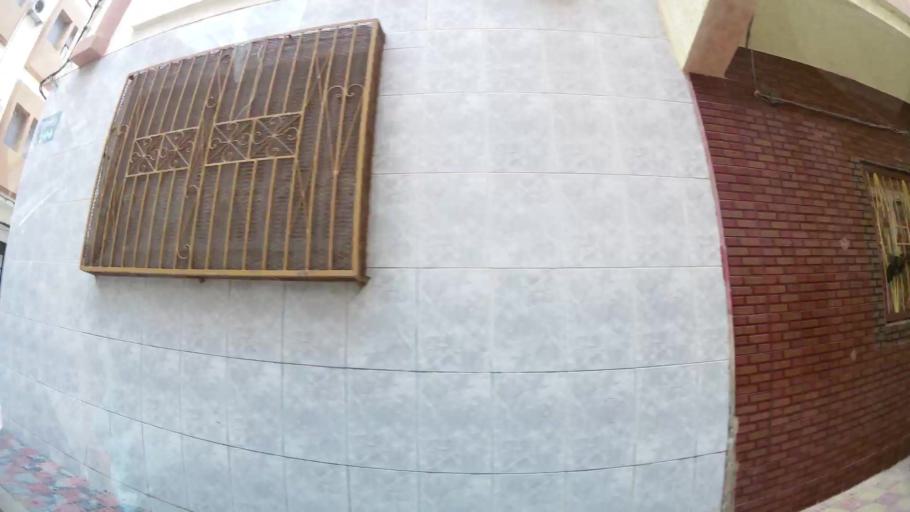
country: MA
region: Oriental
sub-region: Nador
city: Nador
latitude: 35.1626
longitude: -2.9255
